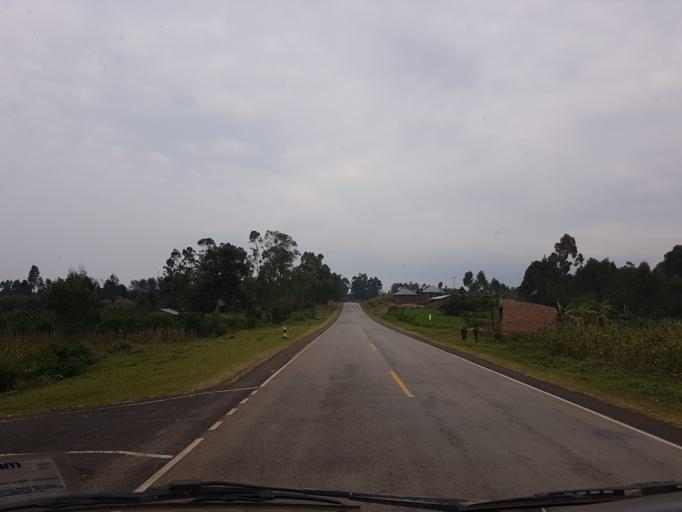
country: UG
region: Western Region
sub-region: Kisoro District
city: Kisoro
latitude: -1.3211
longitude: 29.7283
